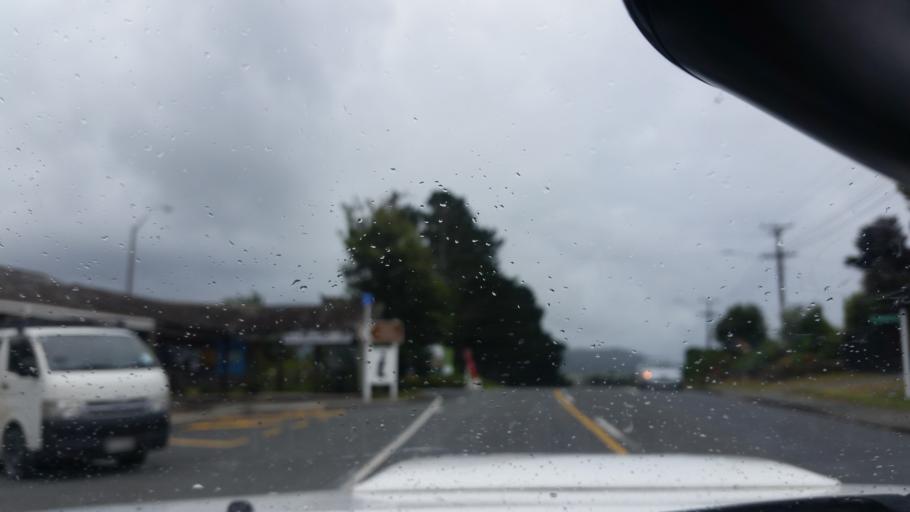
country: NZ
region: Auckland
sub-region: Auckland
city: Wellsford
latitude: -36.0990
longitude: 174.5876
